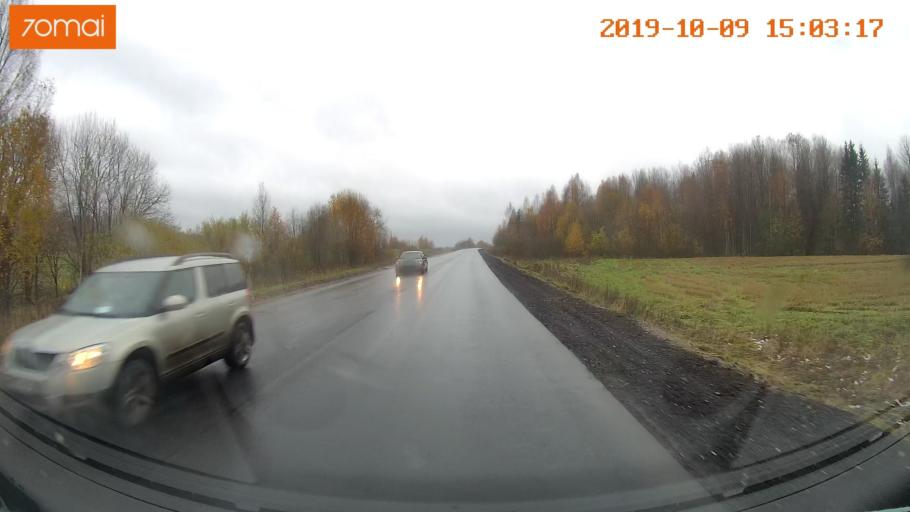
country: RU
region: Kostroma
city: Chistyye Bory
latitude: 58.2733
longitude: 41.6760
